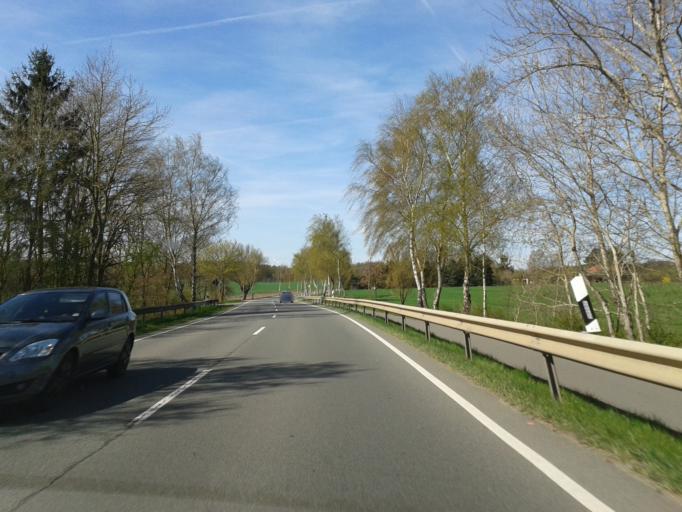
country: DE
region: Lower Saxony
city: Uelzen
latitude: 52.9545
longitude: 10.5294
